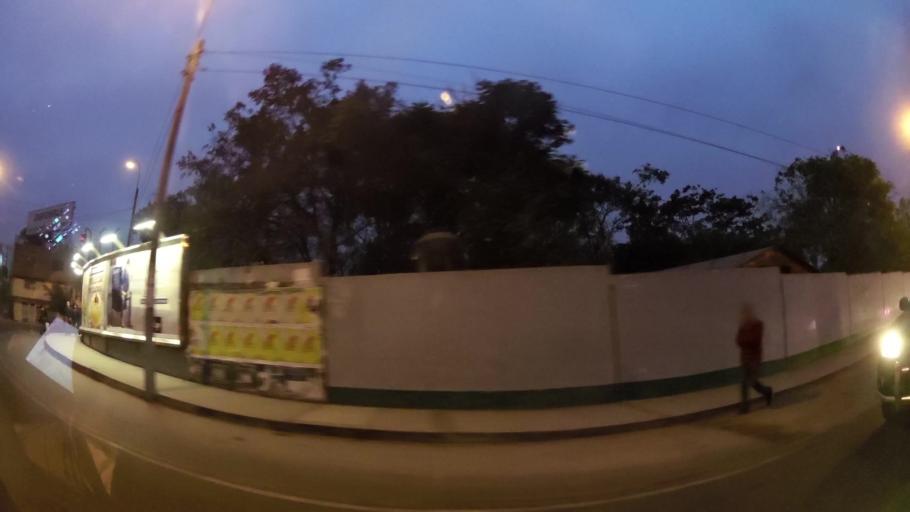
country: PE
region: Lima
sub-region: Lima
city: La Molina
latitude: -12.0772
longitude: -76.9542
